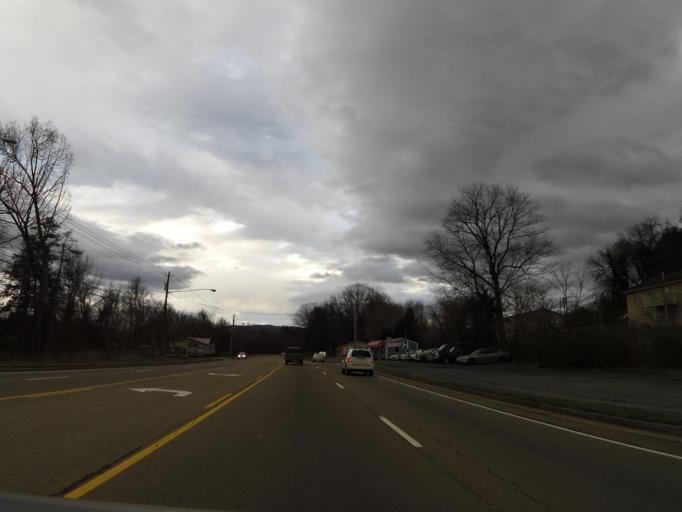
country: US
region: Tennessee
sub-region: Carter County
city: Central
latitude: 36.3385
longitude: -82.2588
